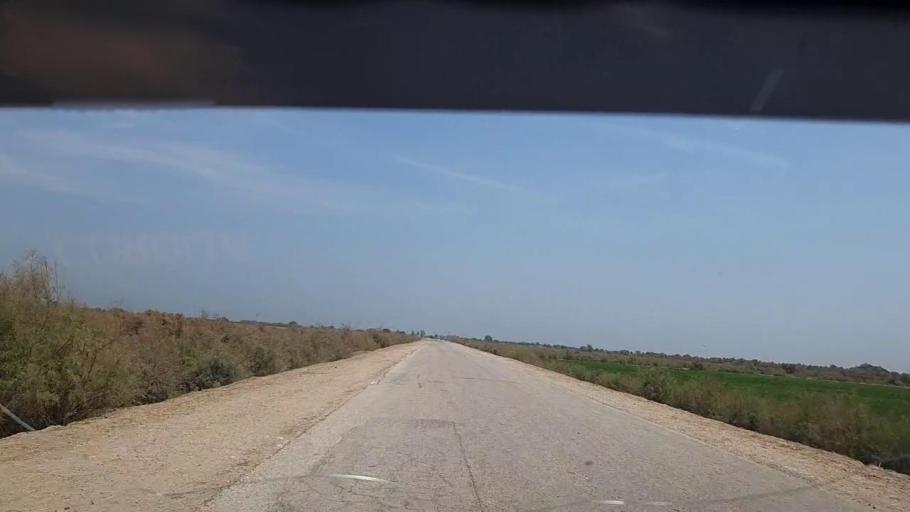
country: PK
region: Sindh
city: Thul
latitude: 28.2070
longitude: 68.8126
